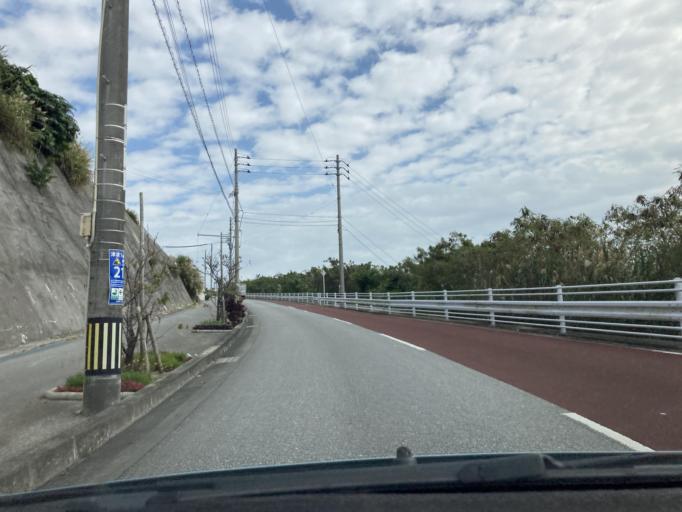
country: JP
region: Okinawa
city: Tomigusuku
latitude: 26.1858
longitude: 127.6898
